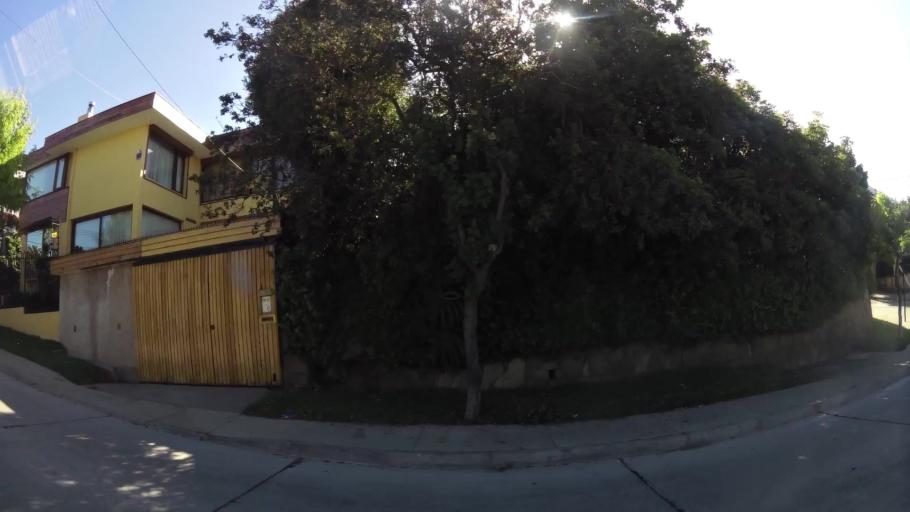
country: CL
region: Valparaiso
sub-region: Provincia de Valparaiso
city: Vina del Mar
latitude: -33.0362
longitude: -71.5567
